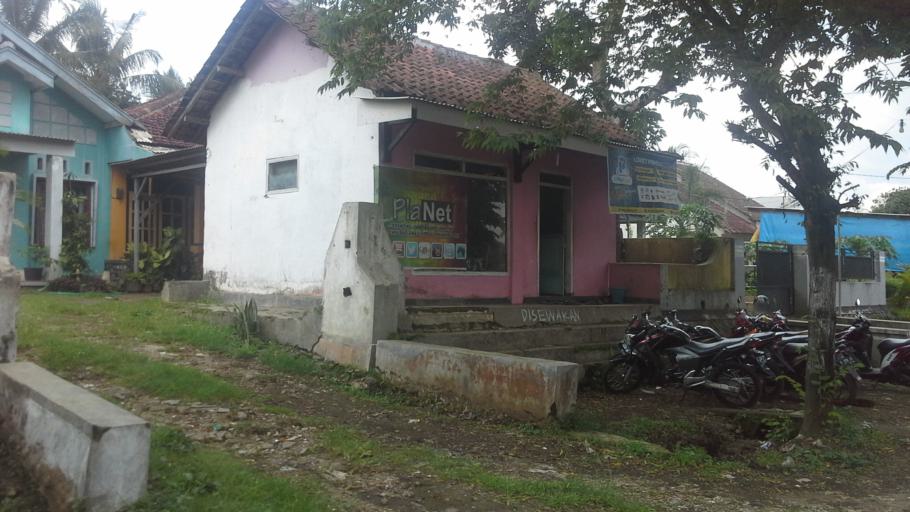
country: ID
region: East Java
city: Krajan Satu Pekauman
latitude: -7.9853
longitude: 113.7931
